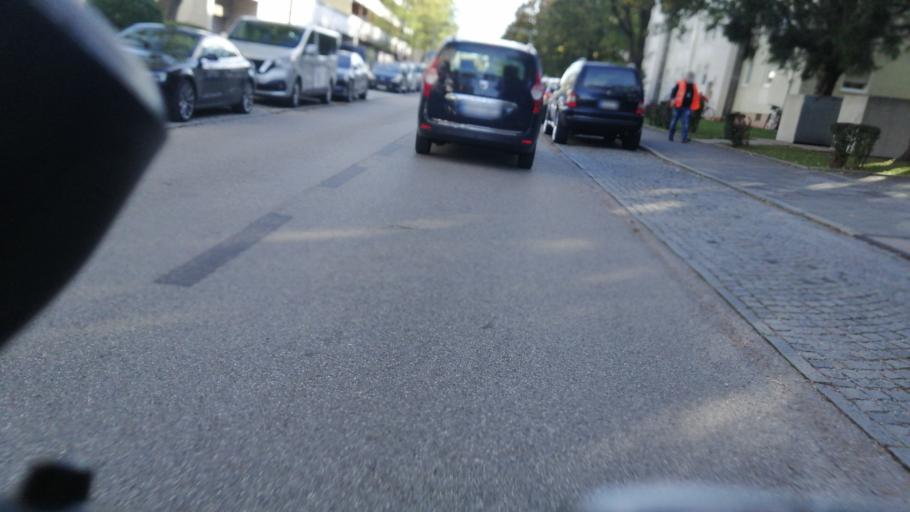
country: DE
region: Bavaria
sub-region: Upper Bavaria
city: Unterfoehring
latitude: 48.1977
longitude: 11.6150
